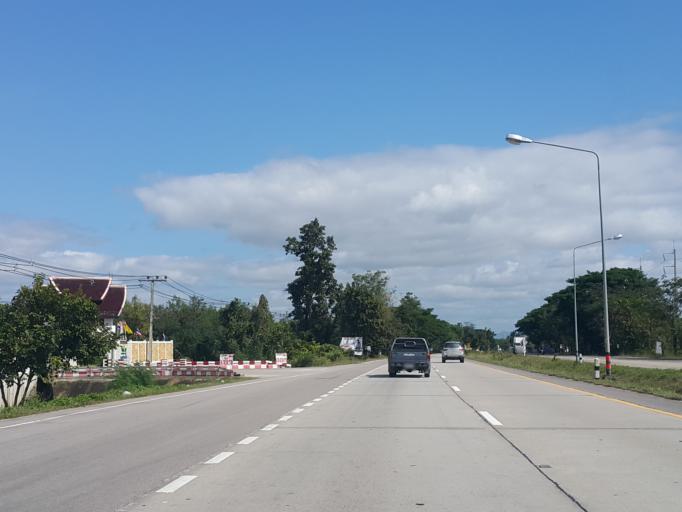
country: TH
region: Lampang
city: Hang Chat
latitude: 18.3213
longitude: 99.3347
